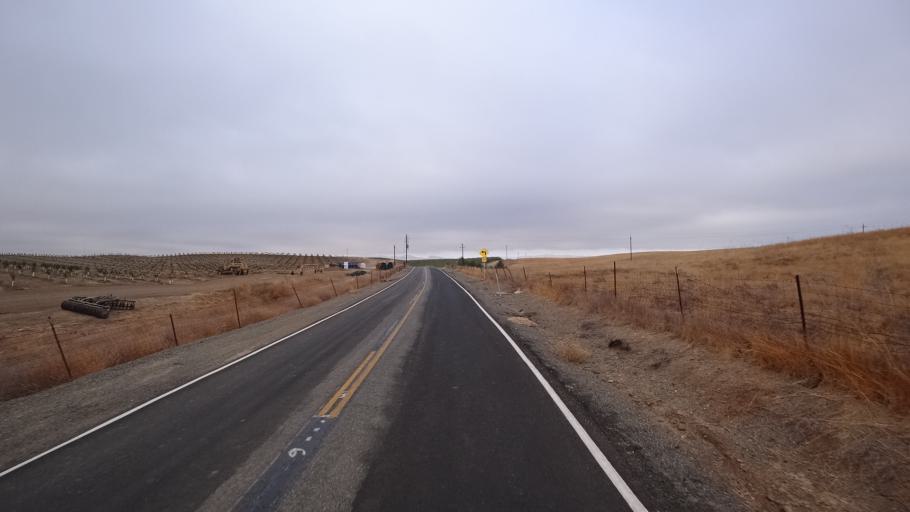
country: US
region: California
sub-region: Yolo County
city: Dunnigan
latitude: 38.8866
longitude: -122.0229
